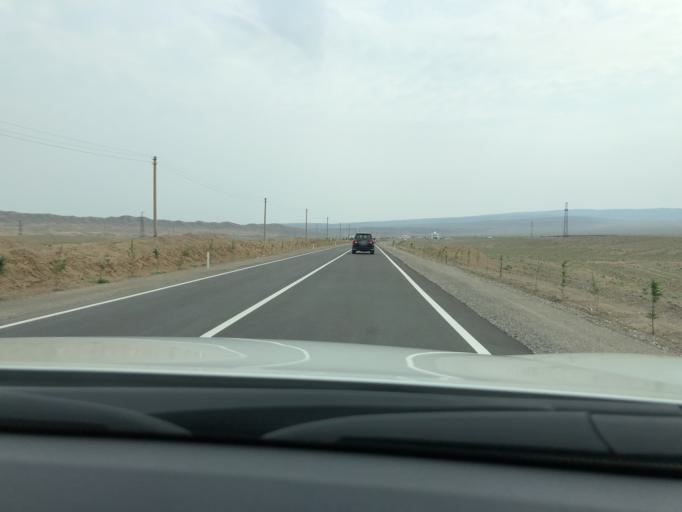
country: TJ
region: Viloyati Sughd
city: Kim
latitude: 40.1962
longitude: 70.4744
